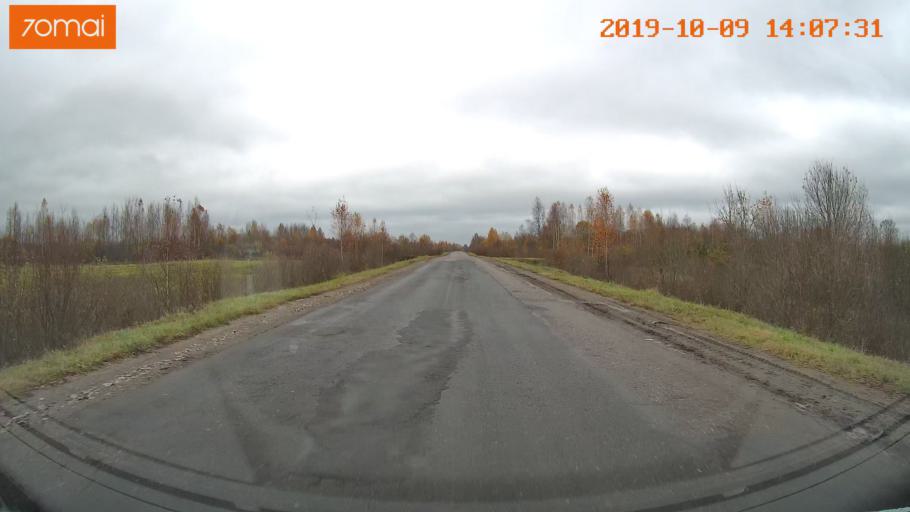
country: RU
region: Kostroma
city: Buy
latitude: 58.4710
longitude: 41.4237
